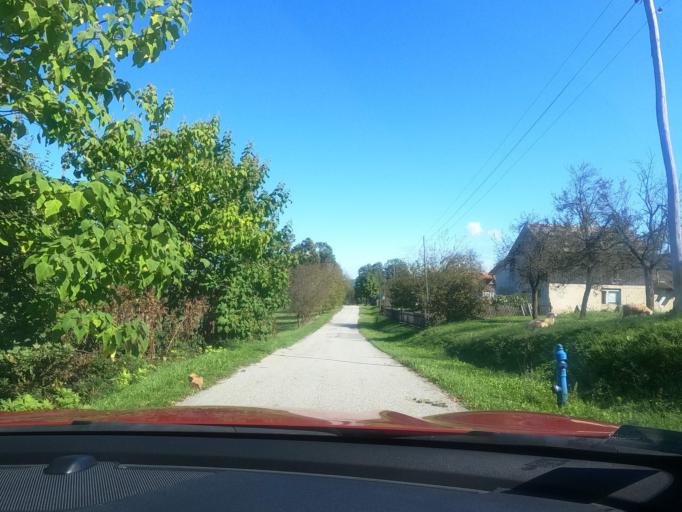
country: HR
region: Sisacko-Moslavacka
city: Glina
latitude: 45.3396
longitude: 16.2107
